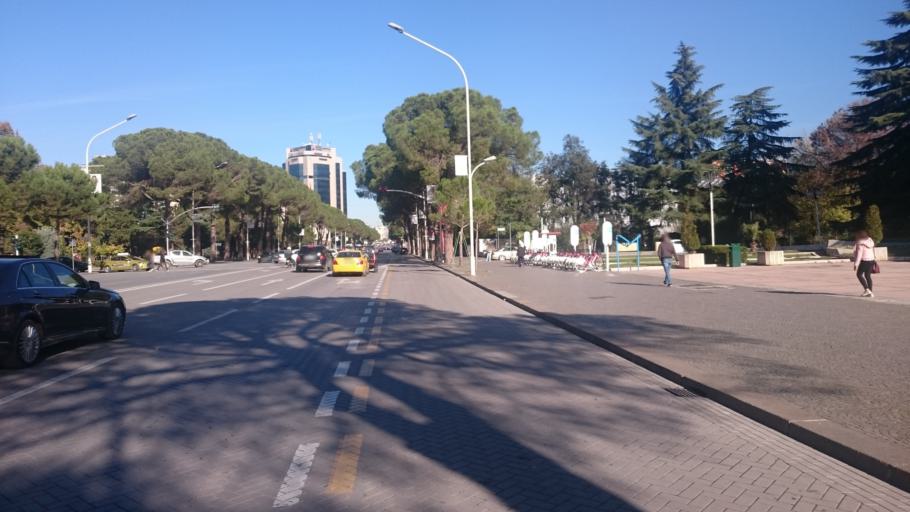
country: AL
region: Tirane
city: Tirana
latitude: 41.3190
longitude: 19.8211
